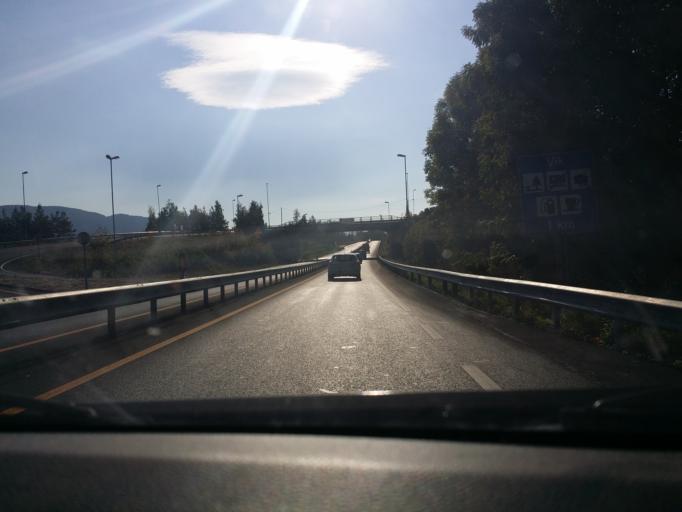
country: NO
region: Buskerud
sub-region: Hole
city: Vik
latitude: 60.0916
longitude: 10.2908
